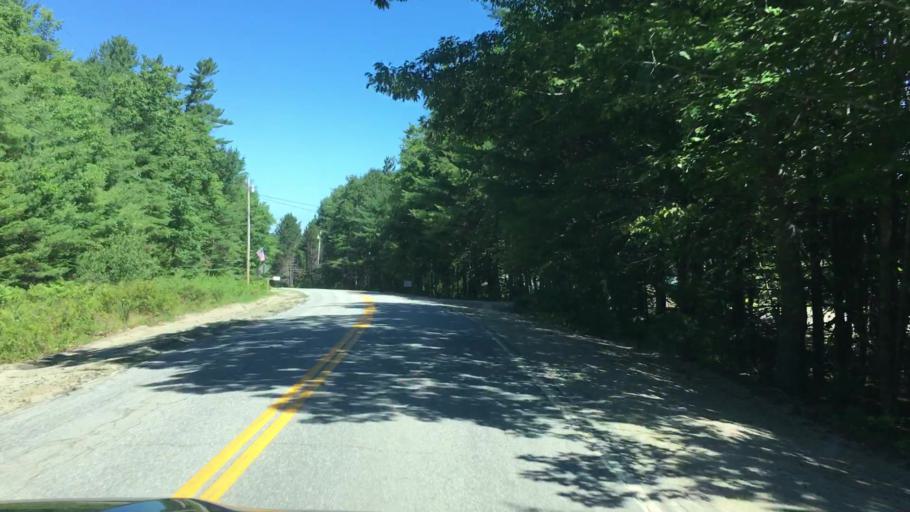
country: US
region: Maine
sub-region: Hancock County
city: Penobscot
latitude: 44.4475
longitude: -68.7018
